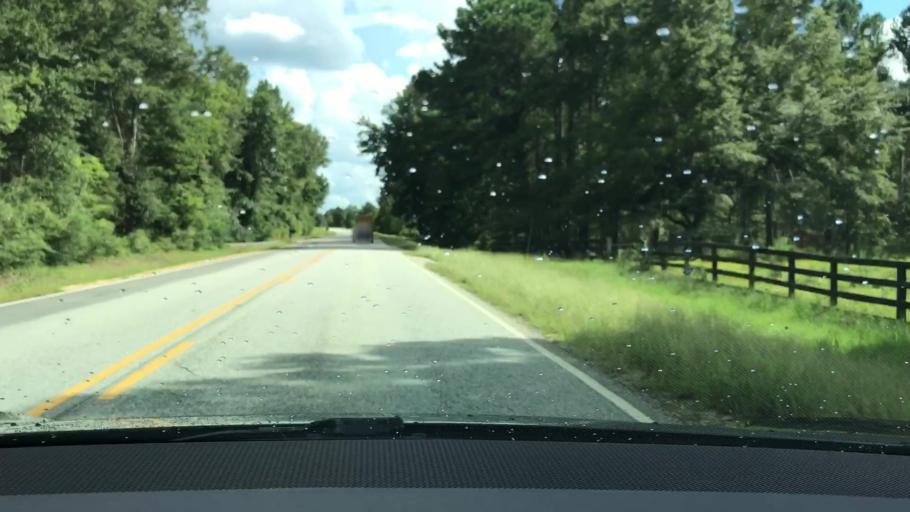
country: US
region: Alabama
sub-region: Montgomery County
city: Pike Road
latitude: 32.2308
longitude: -86.0930
